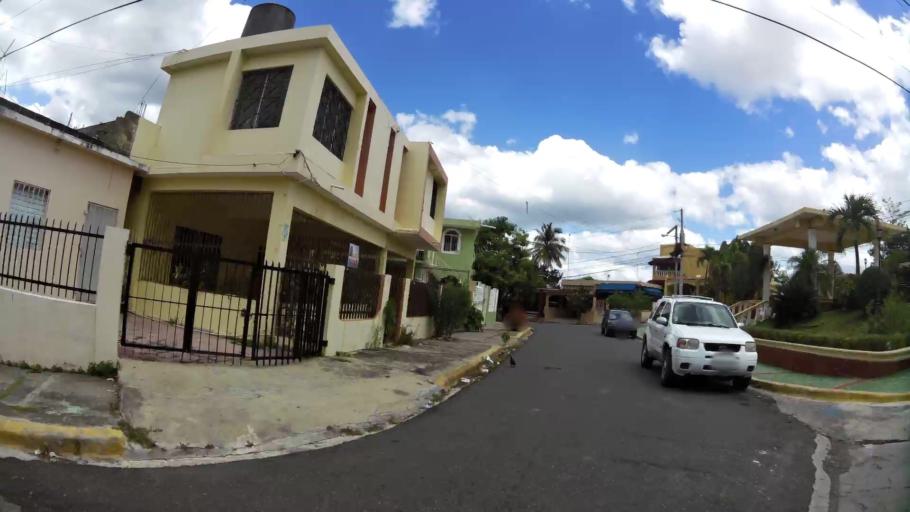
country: DO
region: Nacional
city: Ensanche Luperon
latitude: 18.5166
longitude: -69.9092
